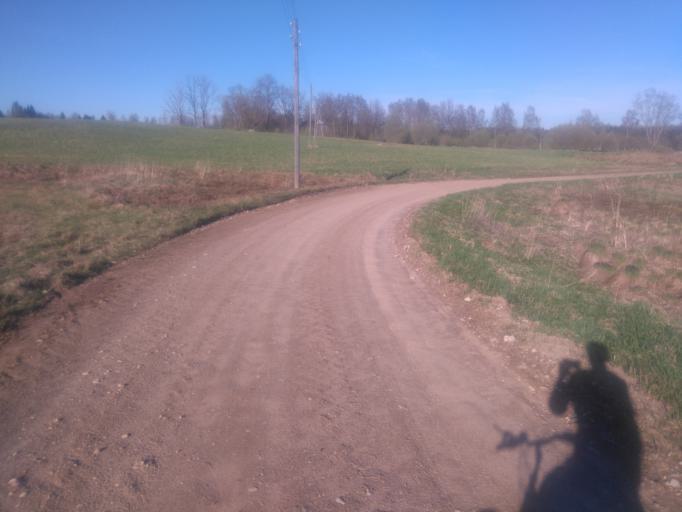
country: LV
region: Vecpiebalga
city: Vecpiebalga
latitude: 57.0255
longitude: 25.8567
